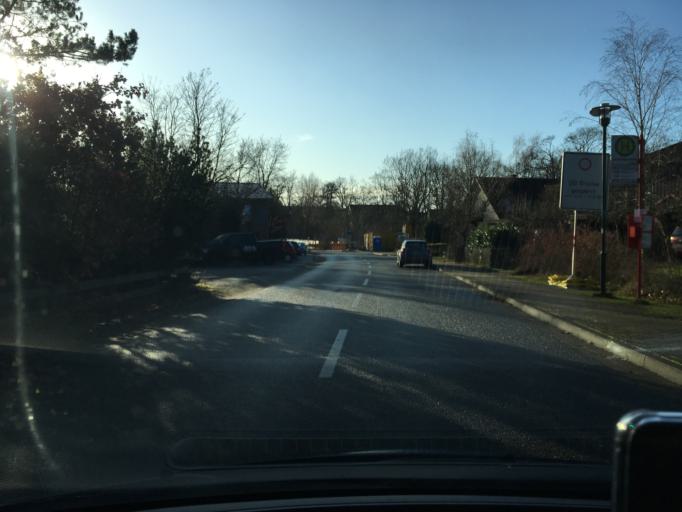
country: DE
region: Lower Saxony
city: Wendisch Evern
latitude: 53.2188
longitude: 10.4696
